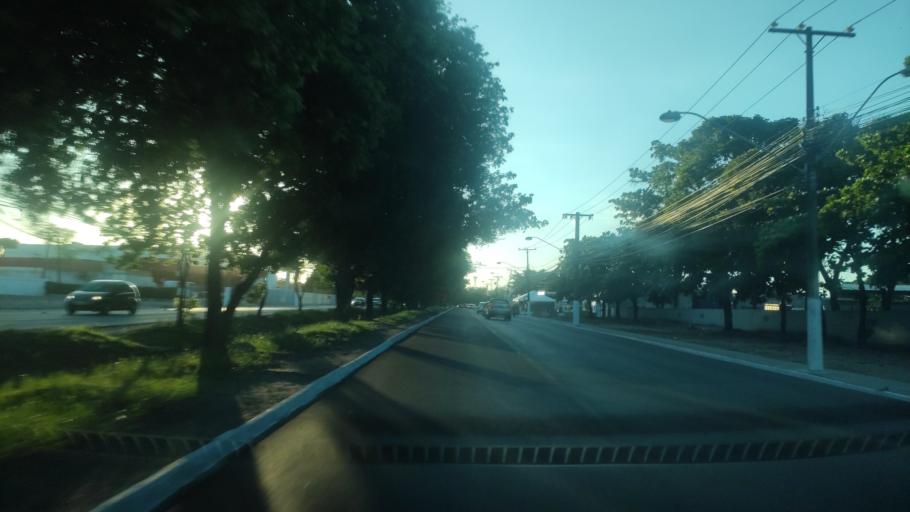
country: BR
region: Alagoas
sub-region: Satuba
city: Satuba
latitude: -9.5919
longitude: -35.7571
